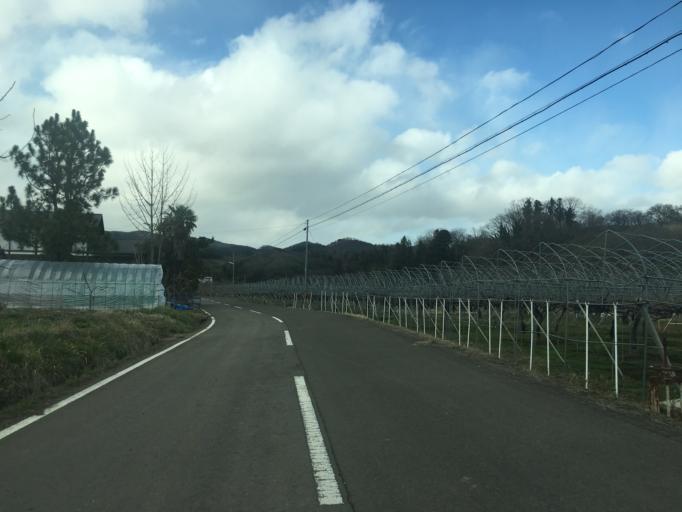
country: JP
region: Fukushima
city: Yanagawamachi-saiwaicho
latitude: 37.8808
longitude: 140.5964
